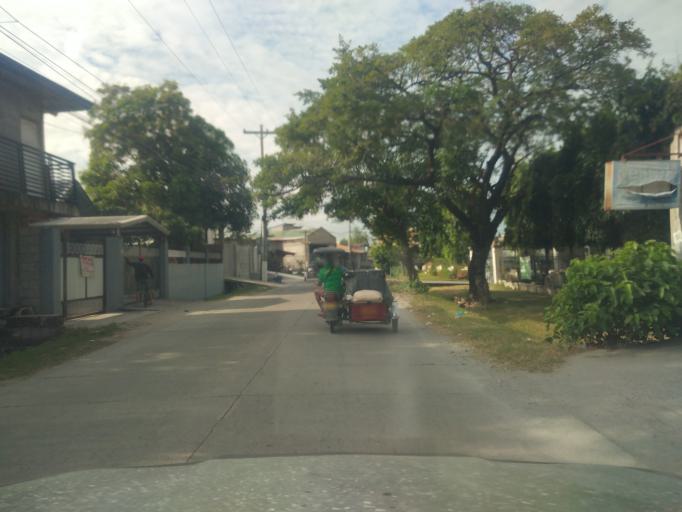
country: PH
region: Central Luzon
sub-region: Province of Pampanga
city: Sexmoan
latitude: 14.9523
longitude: 120.6279
